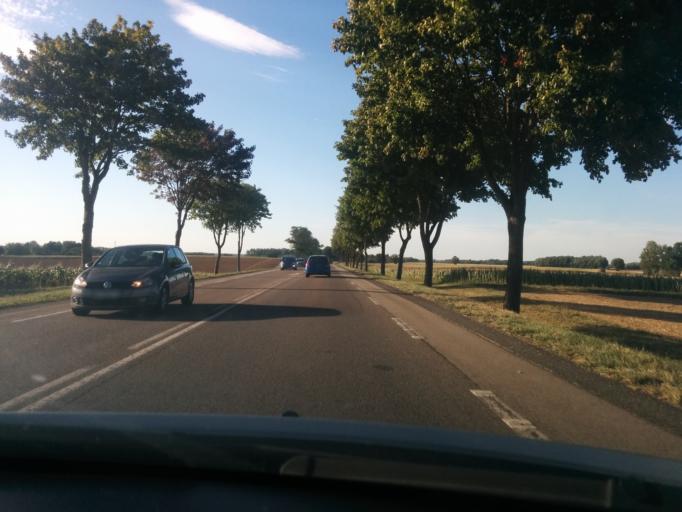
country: FR
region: Rhone-Alpes
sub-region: Departement de l'Ain
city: Tossiat
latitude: 46.1134
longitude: 5.3007
